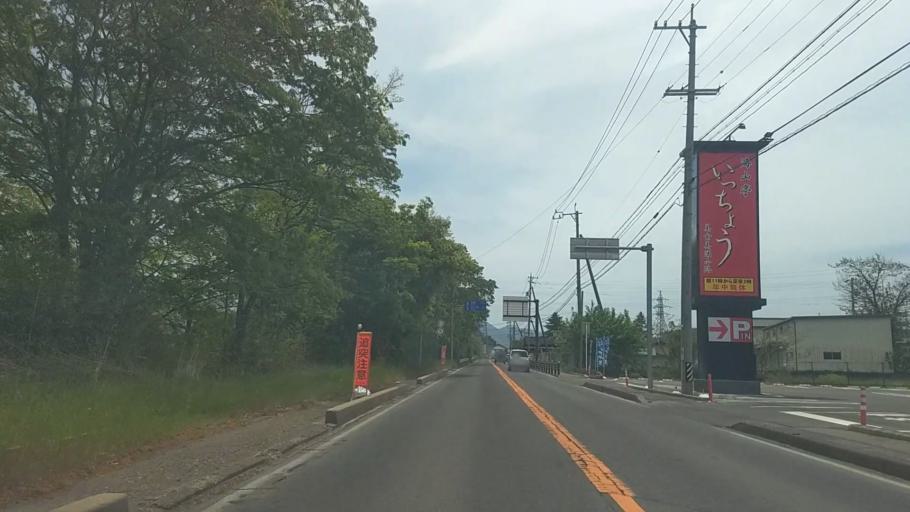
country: JP
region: Nagano
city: Saku
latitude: 36.1885
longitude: 138.4807
